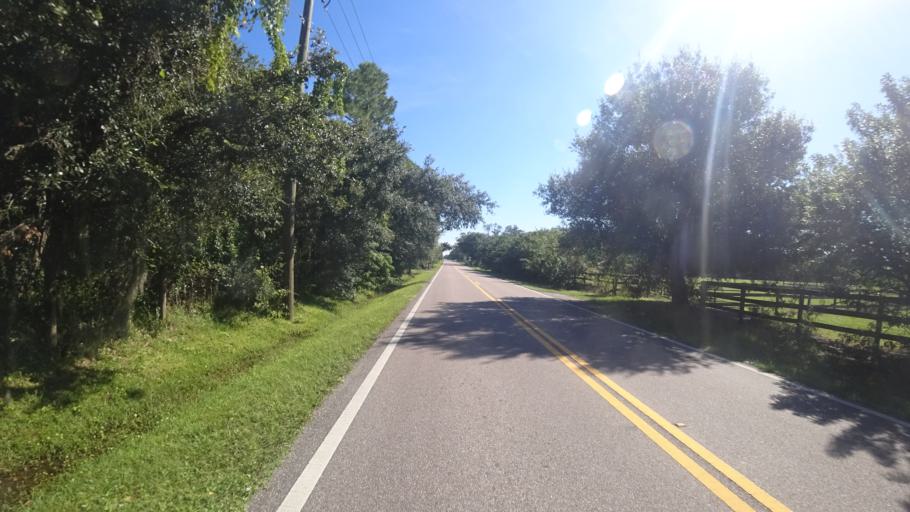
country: US
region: Florida
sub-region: Sarasota County
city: Lake Sarasota
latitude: 27.3501
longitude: -82.2680
